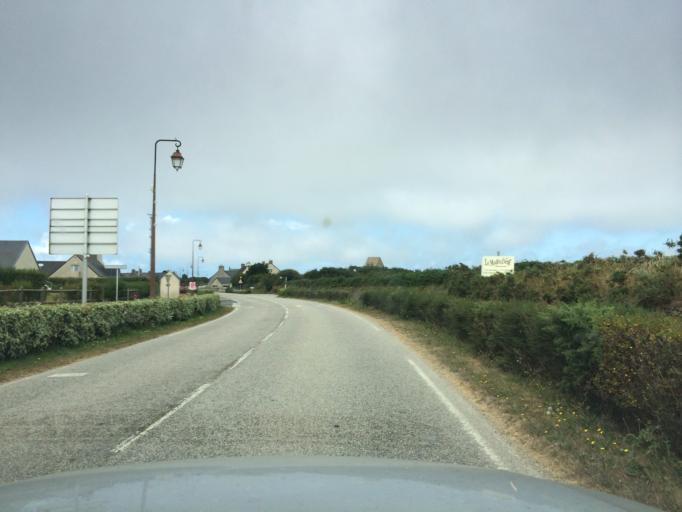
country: FR
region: Lower Normandy
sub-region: Departement de la Manche
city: Beaumont-Hague
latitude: 49.6820
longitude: -1.9021
